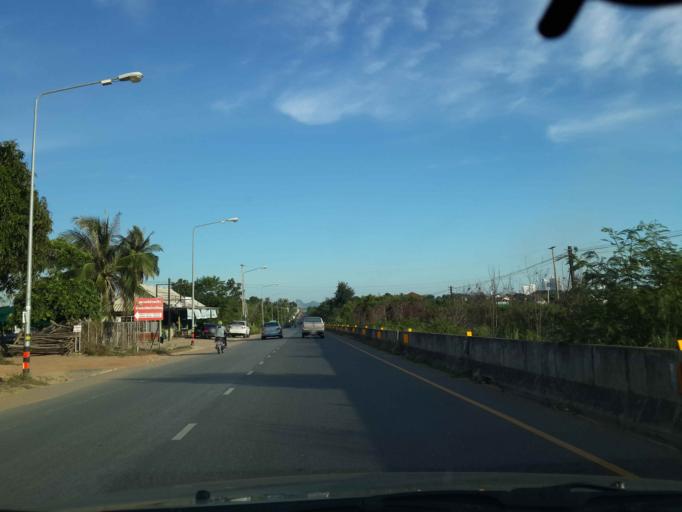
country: TH
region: Chon Buri
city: Phatthaya
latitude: 12.8734
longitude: 100.9083
